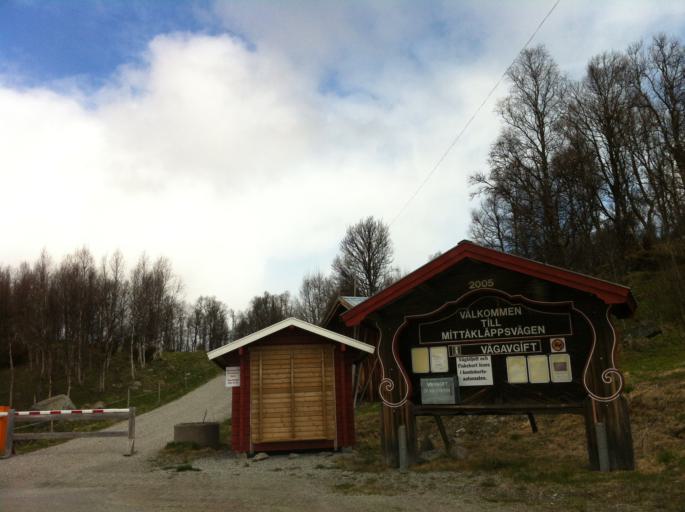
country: NO
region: Sor-Trondelag
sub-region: Tydal
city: Aas
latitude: 62.6401
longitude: 12.4434
